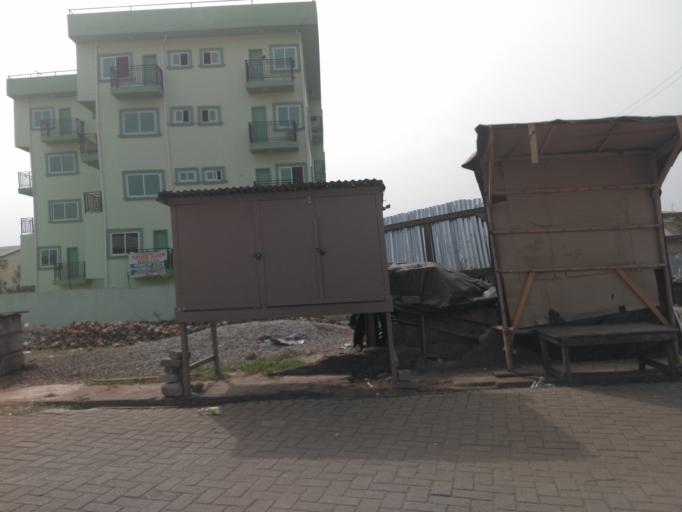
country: GH
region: Ashanti
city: Kumasi
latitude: 6.6916
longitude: -1.6121
